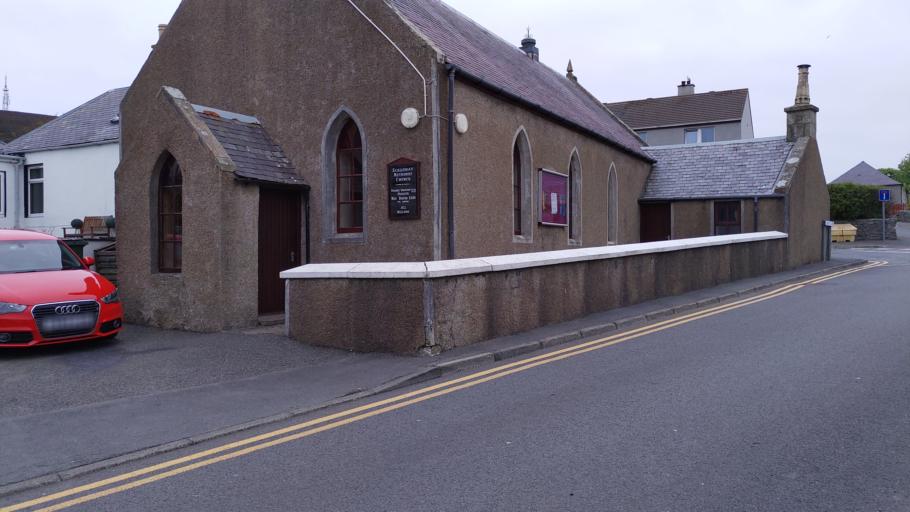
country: GB
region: Scotland
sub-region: Shetland Islands
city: Lerwick
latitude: 60.1380
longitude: -1.2779
